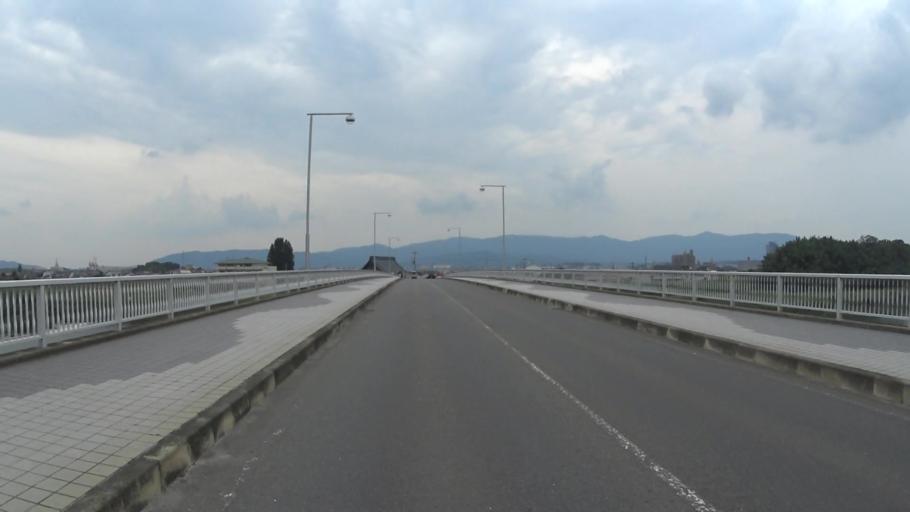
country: JP
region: Kyoto
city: Muko
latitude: 34.9454
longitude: 135.7369
